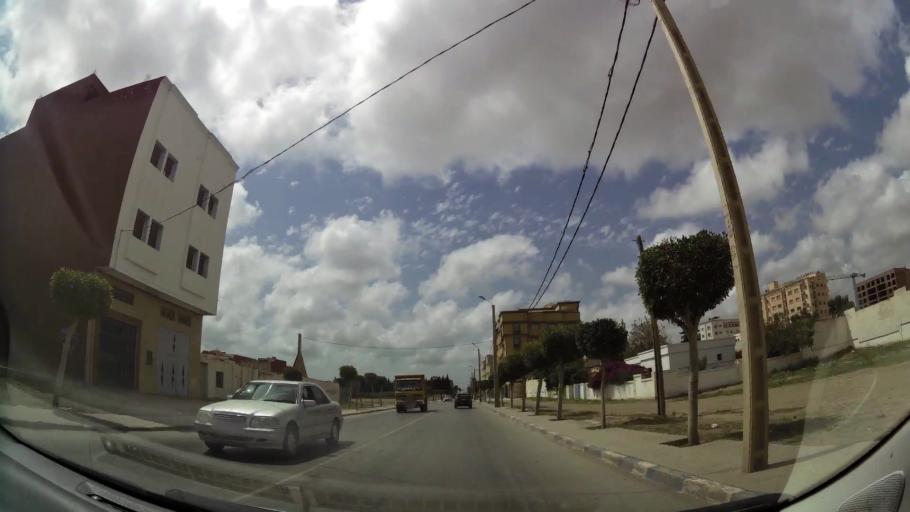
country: MA
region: Oriental
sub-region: Nador
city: Nador
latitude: 35.1608
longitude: -2.9288
